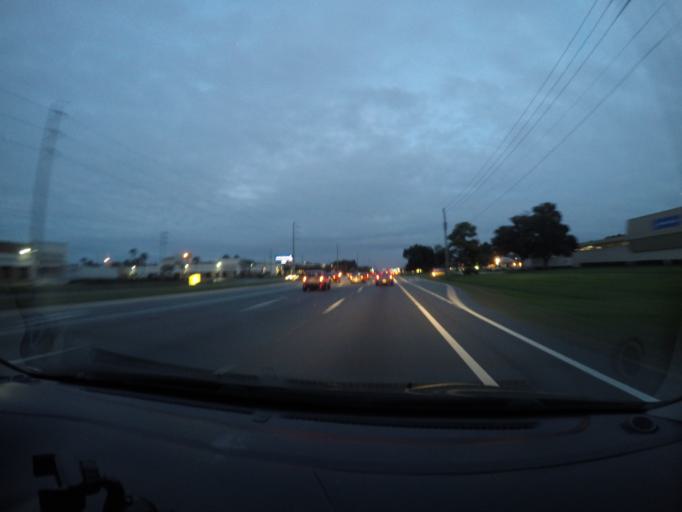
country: US
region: Florida
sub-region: Orange County
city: Sky Lake
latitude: 28.4503
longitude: -81.4106
